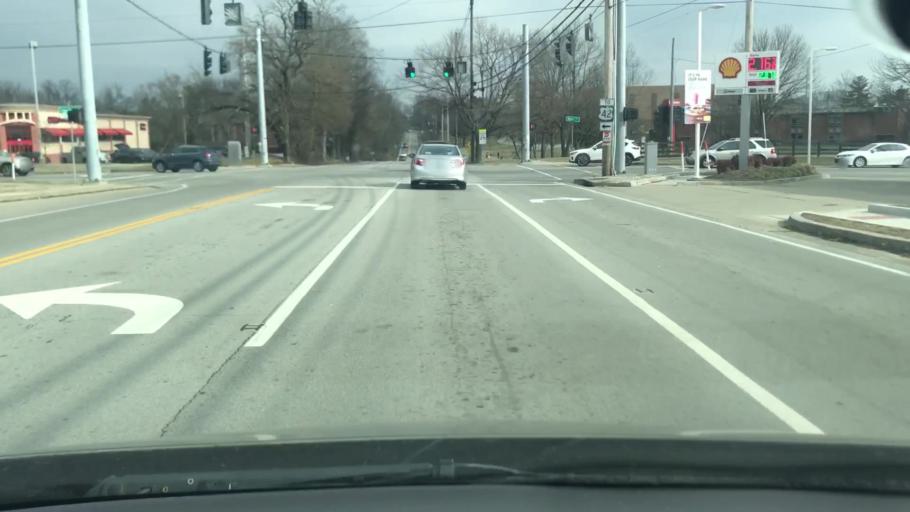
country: US
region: Kentucky
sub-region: Jefferson County
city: Windy Hills
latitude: 38.2837
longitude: -85.6284
